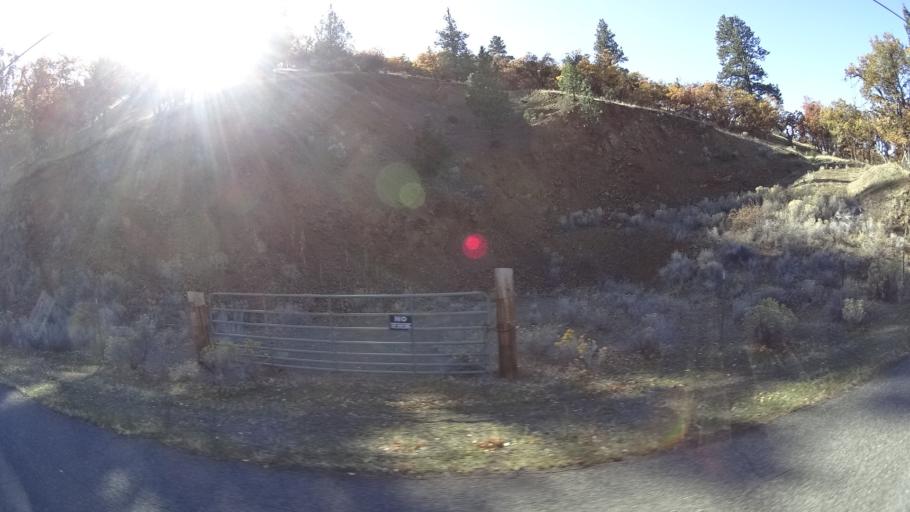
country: US
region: California
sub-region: Siskiyou County
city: Montague
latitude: 41.9794
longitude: -122.3131
